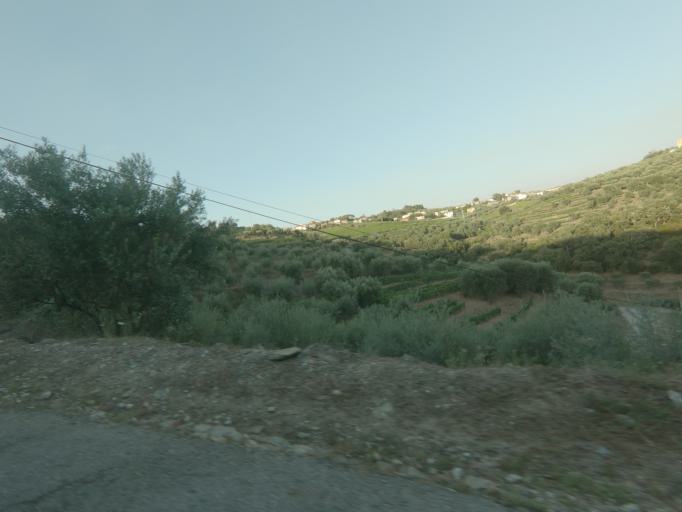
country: PT
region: Viseu
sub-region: Armamar
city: Armamar
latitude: 41.1815
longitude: -7.6903
